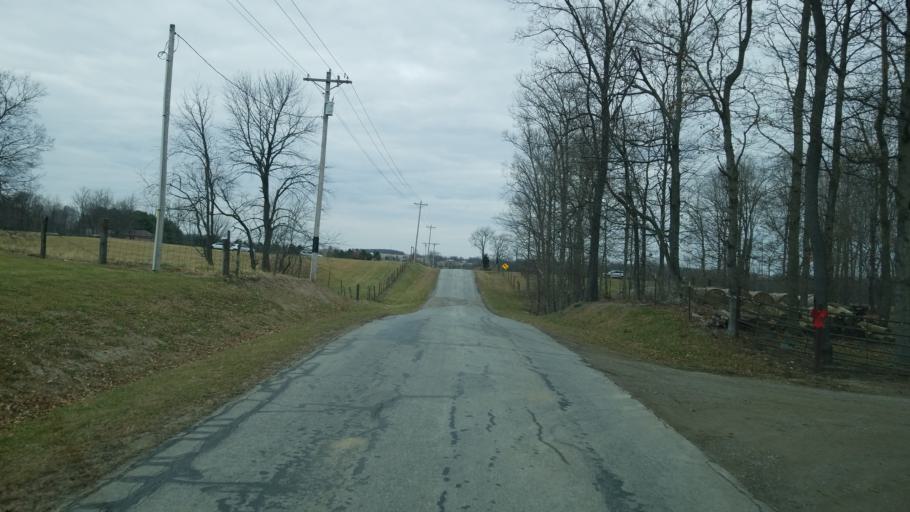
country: US
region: Ohio
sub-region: Highland County
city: Hillsboro
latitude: 39.2184
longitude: -83.4858
